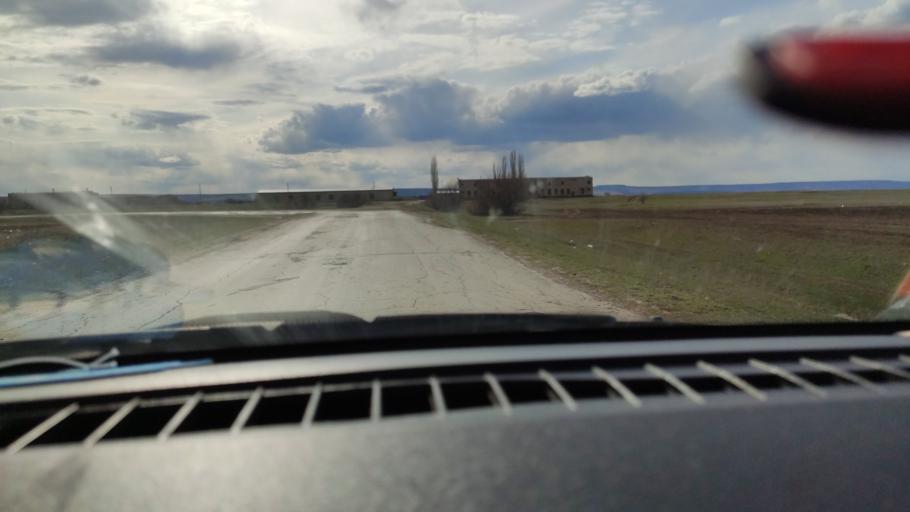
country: RU
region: Saratov
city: Rovnoye
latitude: 50.9362
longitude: 46.0944
